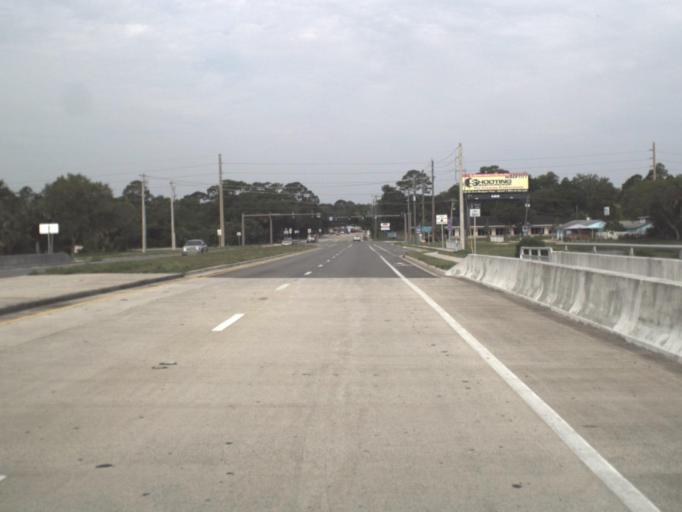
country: US
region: Florida
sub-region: Saint Johns County
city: Saint Augustine
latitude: 29.9161
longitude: -81.3285
